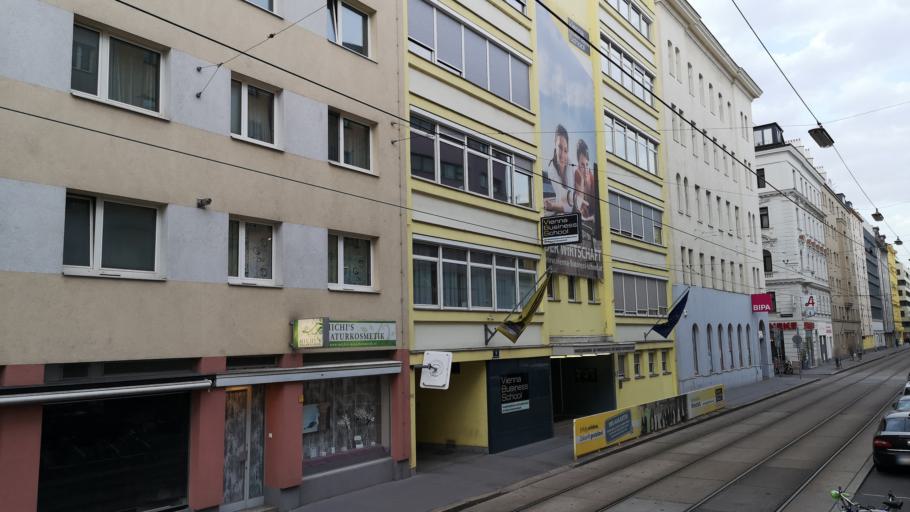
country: AT
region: Vienna
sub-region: Wien Stadt
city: Vienna
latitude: 48.2202
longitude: 16.3721
